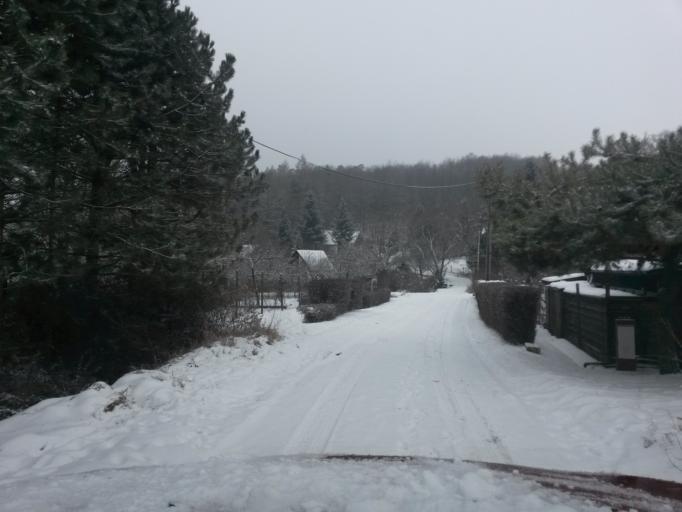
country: SK
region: Kosicky
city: Kosice
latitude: 48.7241
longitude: 21.3039
